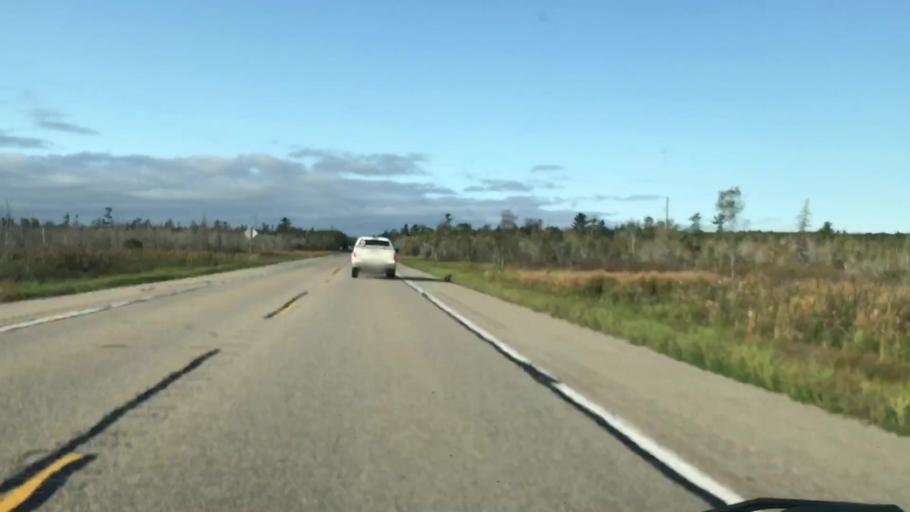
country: US
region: Michigan
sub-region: Luce County
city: Newberry
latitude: 46.3164
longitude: -85.1975
